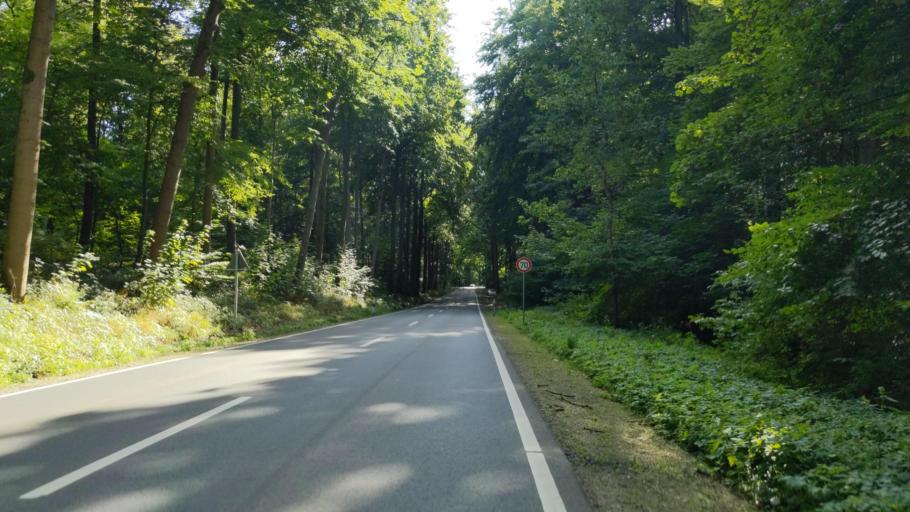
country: DE
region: Schleswig-Holstein
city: Kasseedorf
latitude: 54.1523
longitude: 10.7136
